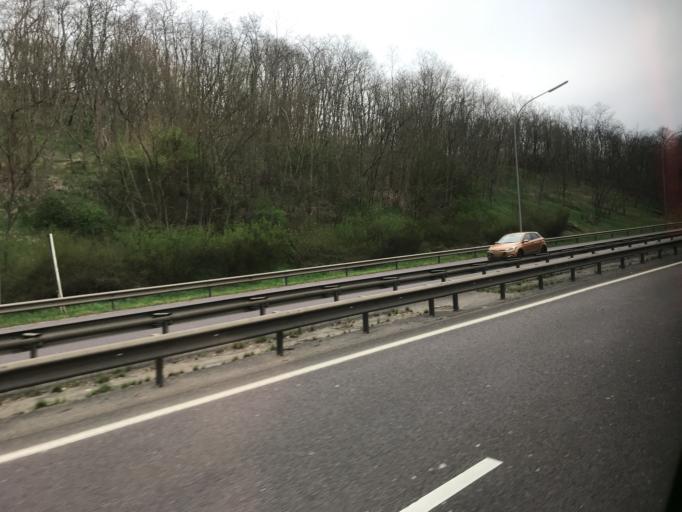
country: LU
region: Luxembourg
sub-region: Canton d'Esch-sur-Alzette
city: Leudelange
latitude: 49.5799
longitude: 6.0878
